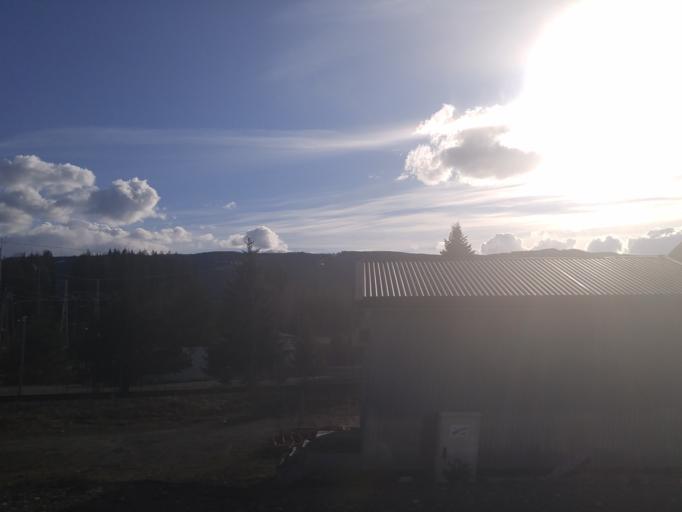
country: NO
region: Oppland
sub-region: Lillehammer
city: Lillehammer
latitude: 61.1395
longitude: 10.4220
